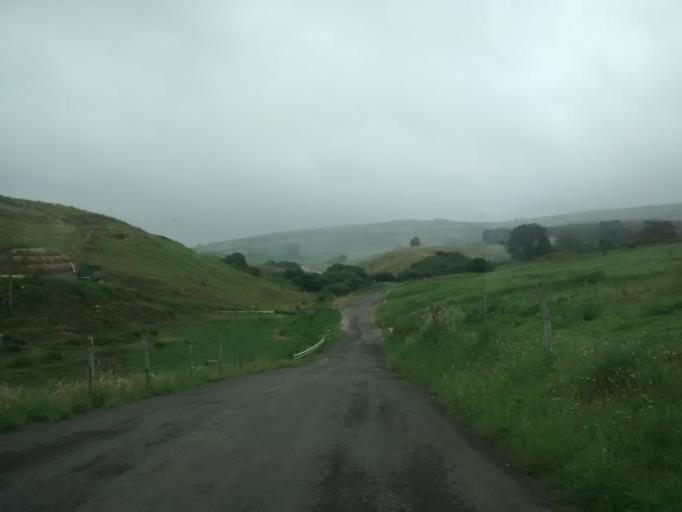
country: ES
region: Cantabria
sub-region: Provincia de Cantabria
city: Santillana
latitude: 43.4222
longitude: -4.0977
